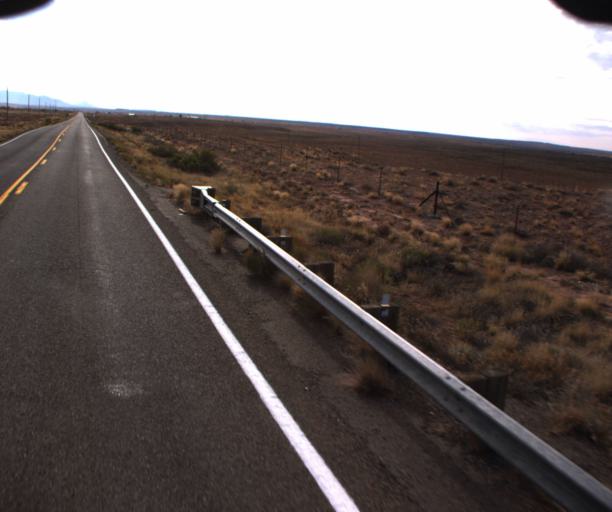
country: US
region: Arizona
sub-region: Apache County
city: Many Farms
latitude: 36.5248
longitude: -109.4978
